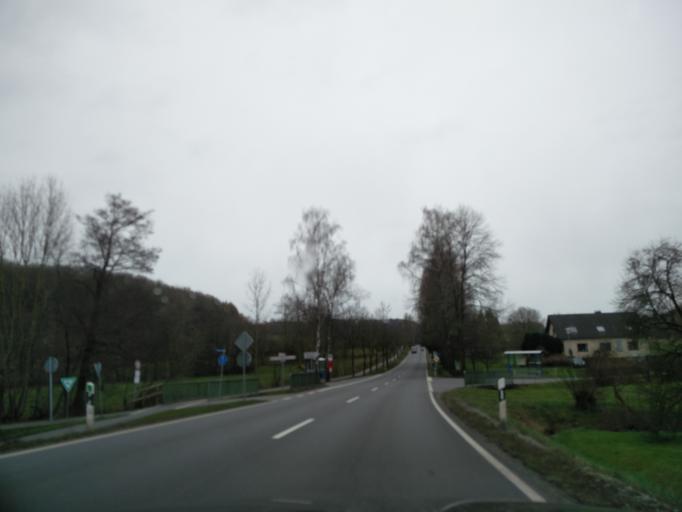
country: DE
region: North Rhine-Westphalia
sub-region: Regierungsbezirk Detmold
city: Horn
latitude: 51.8570
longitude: 8.9604
